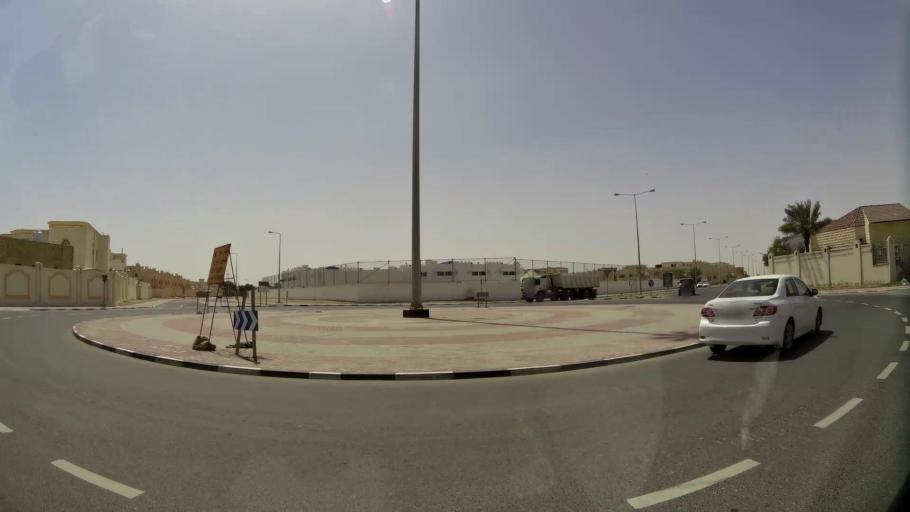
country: QA
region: Baladiyat Umm Salal
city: Umm Salal Muhammad
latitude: 25.3656
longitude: 51.4313
